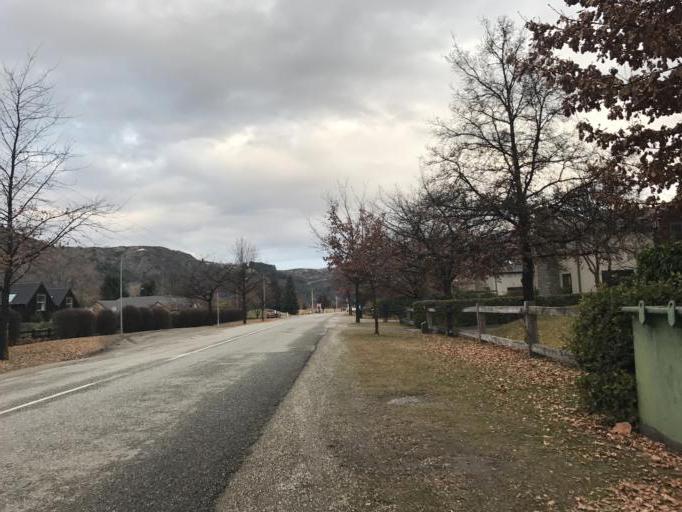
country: NZ
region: Otago
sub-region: Queenstown-Lakes District
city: Arrowtown
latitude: -44.9507
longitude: 168.8423
